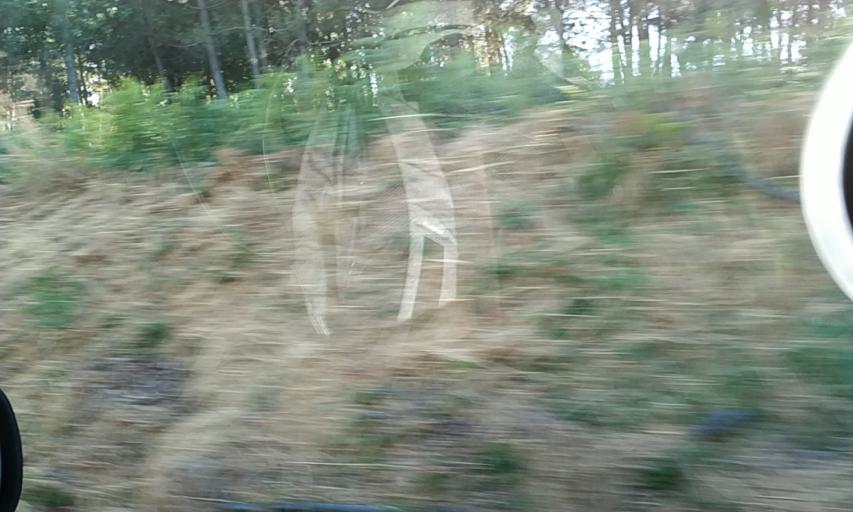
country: PT
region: Vila Real
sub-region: Murca
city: Murca
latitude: 41.3757
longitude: -7.5451
